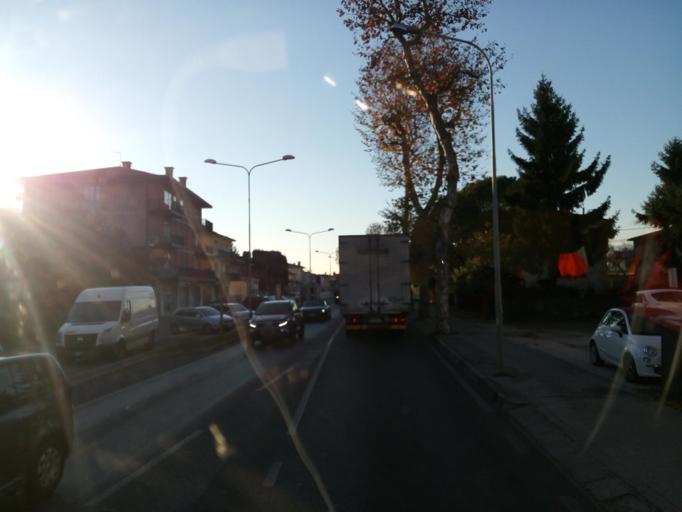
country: IT
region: Veneto
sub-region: Provincia di Treviso
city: Asolo
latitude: 45.7896
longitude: 11.9203
